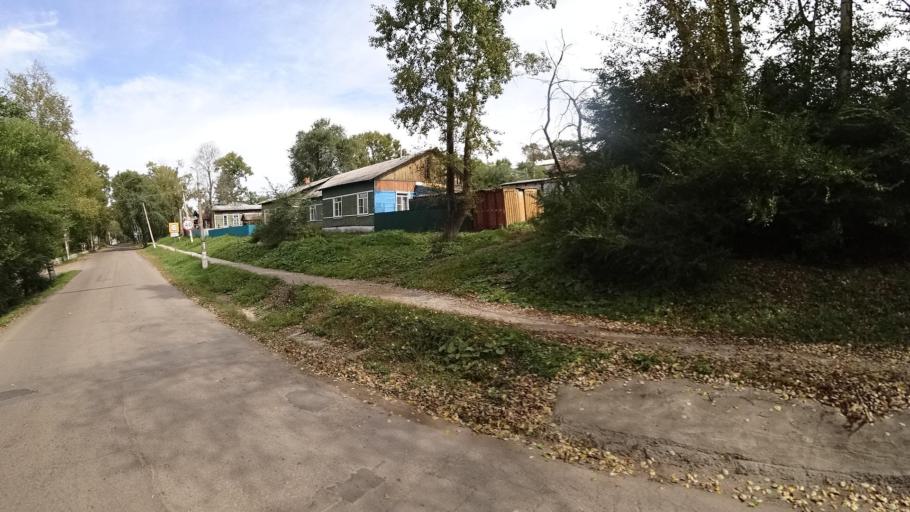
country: RU
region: Jewish Autonomous Oblast
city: Khingansk
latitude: 49.0113
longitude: 131.0605
